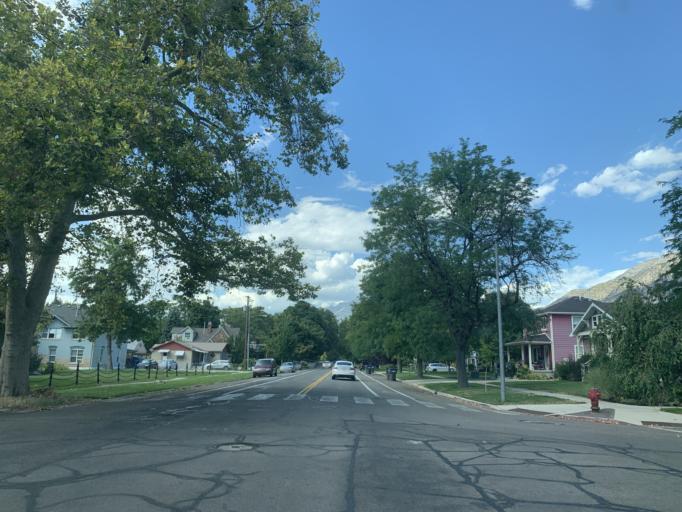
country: US
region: Utah
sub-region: Utah County
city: Provo
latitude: 40.2309
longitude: -111.6517
